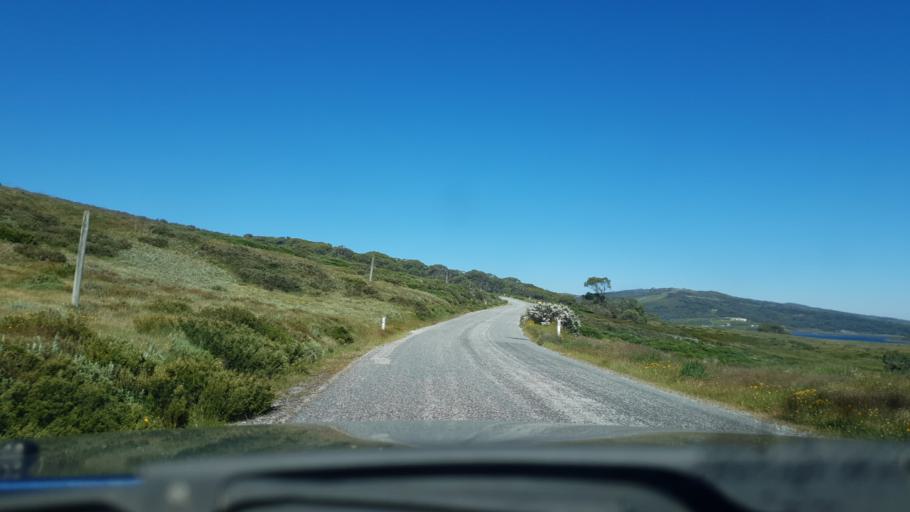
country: AU
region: Victoria
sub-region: Alpine
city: Mount Beauty
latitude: -36.8835
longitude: 147.3133
